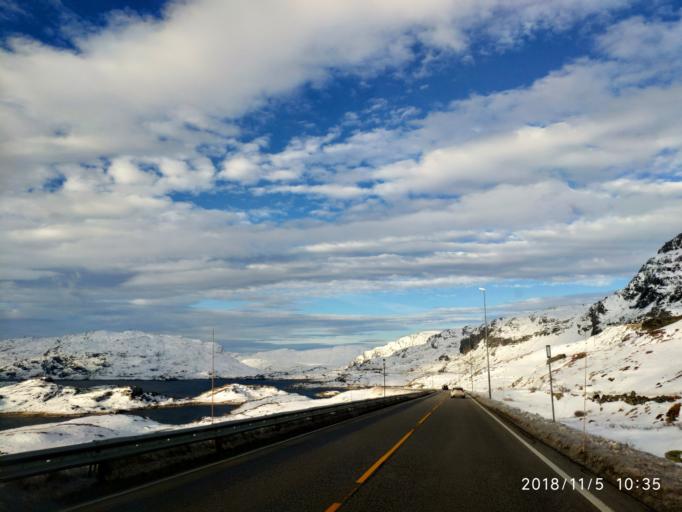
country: NO
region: Aust-Agder
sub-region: Bykle
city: Hovden
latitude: 59.8409
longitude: 6.9822
